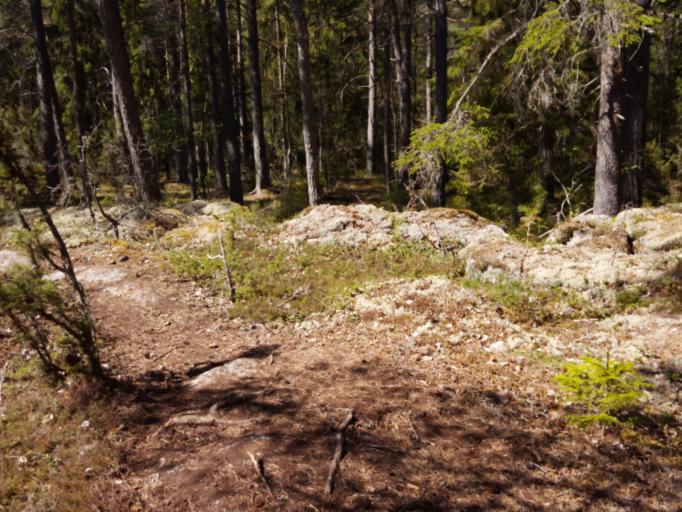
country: SE
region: Uppsala
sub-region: Uppsala Kommun
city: Storvreta
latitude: 59.9031
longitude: 17.7474
